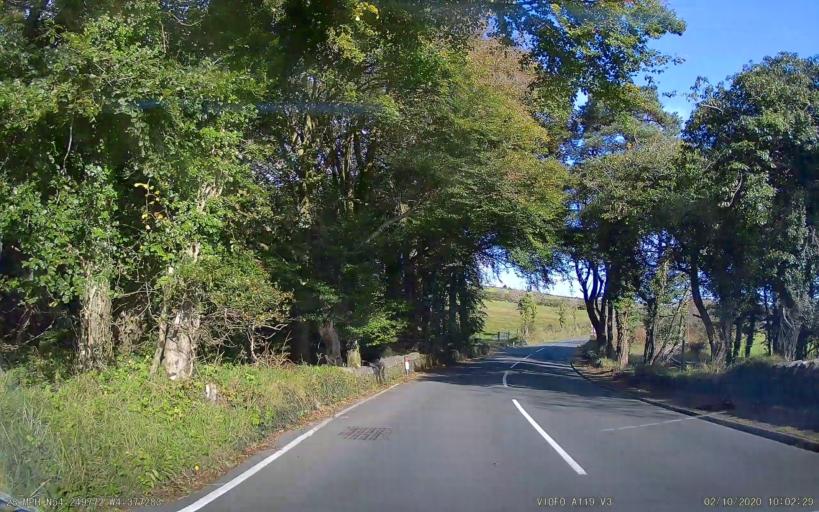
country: IM
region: Laxey
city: Laxey
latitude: 54.2498
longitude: -4.3773
